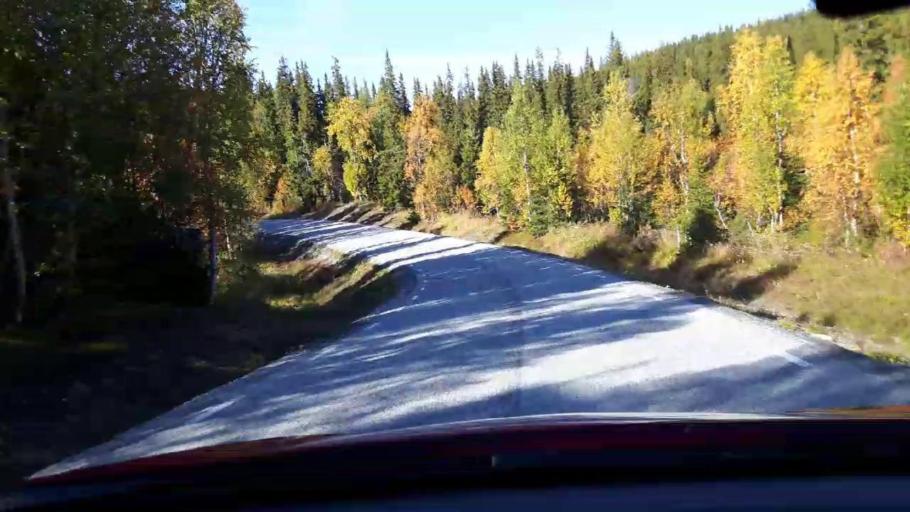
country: NO
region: Nord-Trondelag
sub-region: Royrvik
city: Royrvik
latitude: 64.8153
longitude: 14.1998
